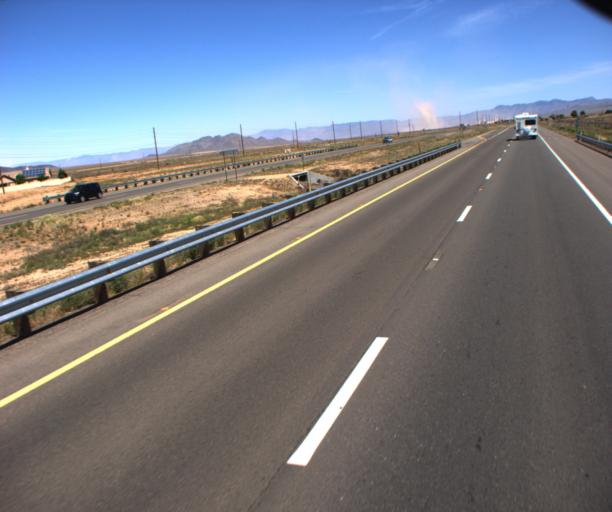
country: US
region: Arizona
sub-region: Mohave County
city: New Kingman-Butler
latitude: 35.2656
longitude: -113.9640
